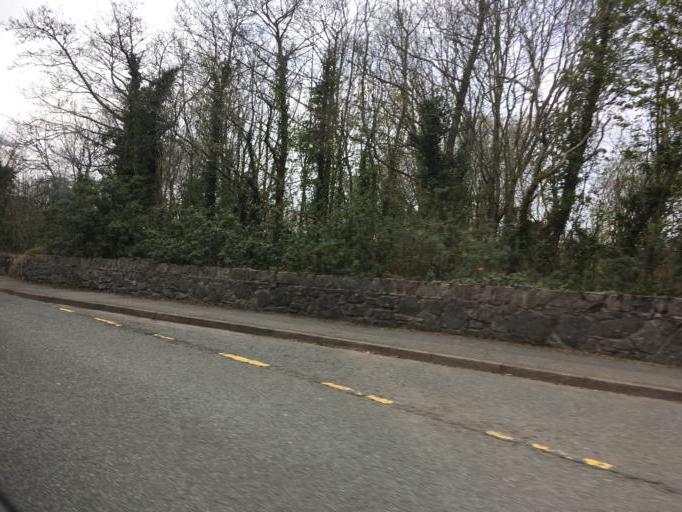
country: GB
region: Wales
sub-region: Gwynedd
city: Y Felinheli
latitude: 53.1781
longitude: -4.2186
